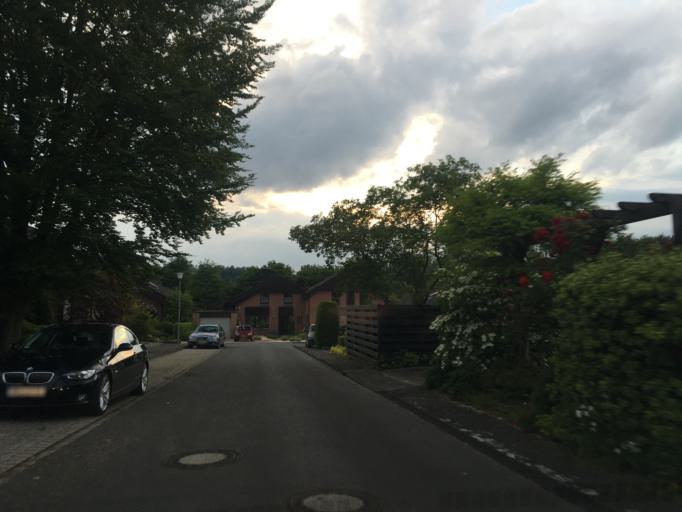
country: DE
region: North Rhine-Westphalia
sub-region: Regierungsbezirk Munster
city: Muenster
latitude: 51.9918
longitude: 7.5870
